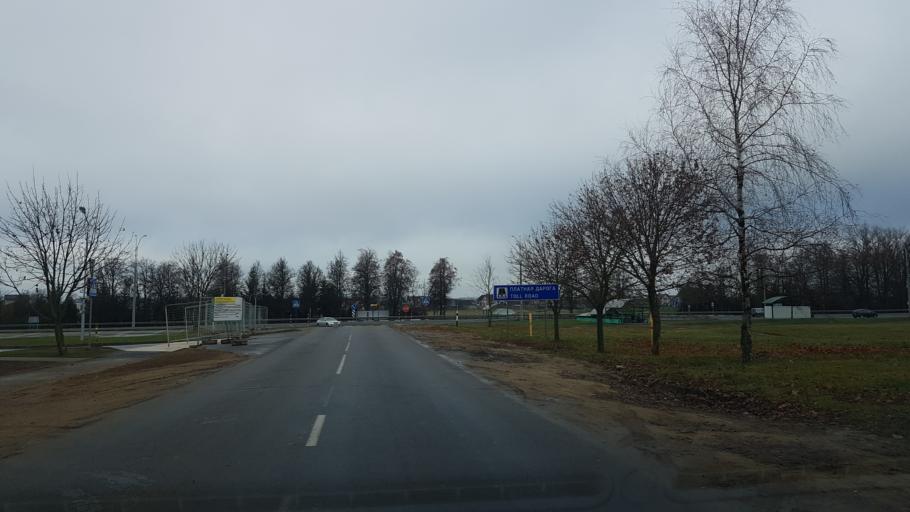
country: BY
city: Fanipol
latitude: 53.7511
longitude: 27.3274
